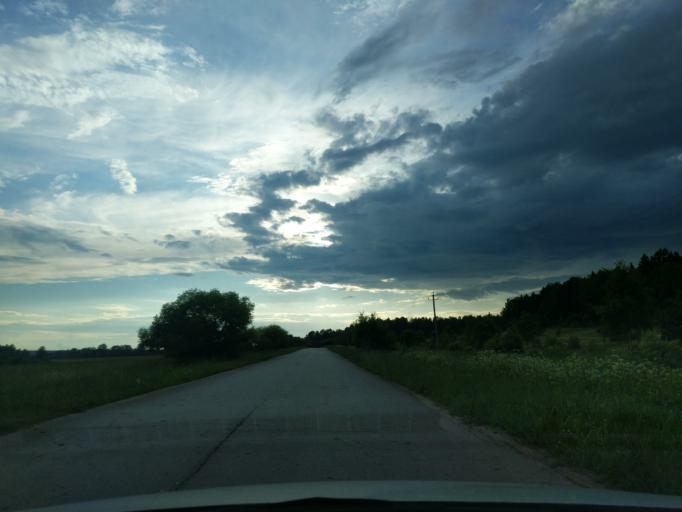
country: RU
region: Kaluga
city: Myatlevo
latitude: 54.8396
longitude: 35.6329
